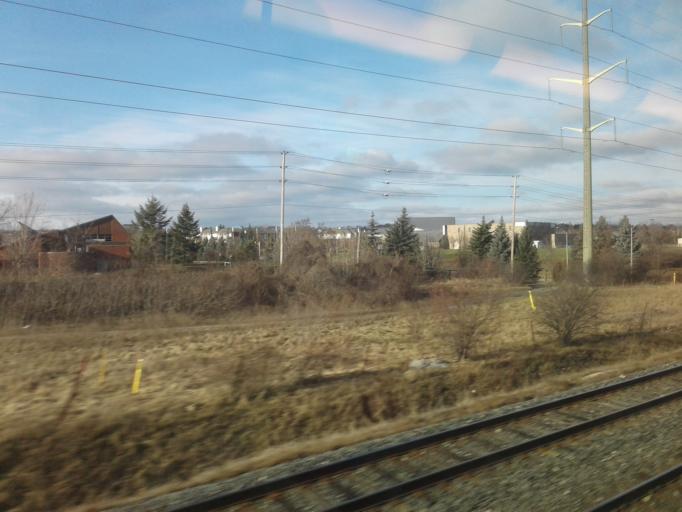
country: CA
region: Ontario
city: Oakville
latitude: 43.4895
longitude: -79.6544
